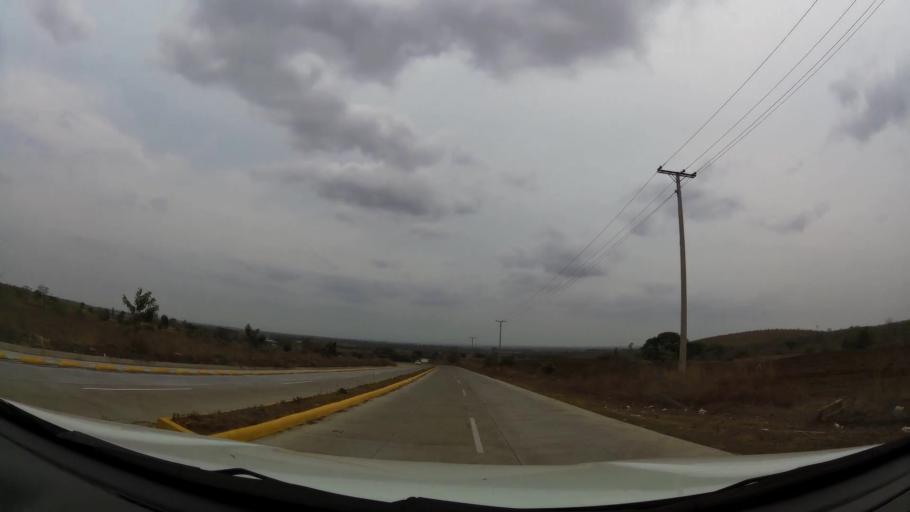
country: NI
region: Masaya
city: Ticuantepe
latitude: 12.0963
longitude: -86.1769
